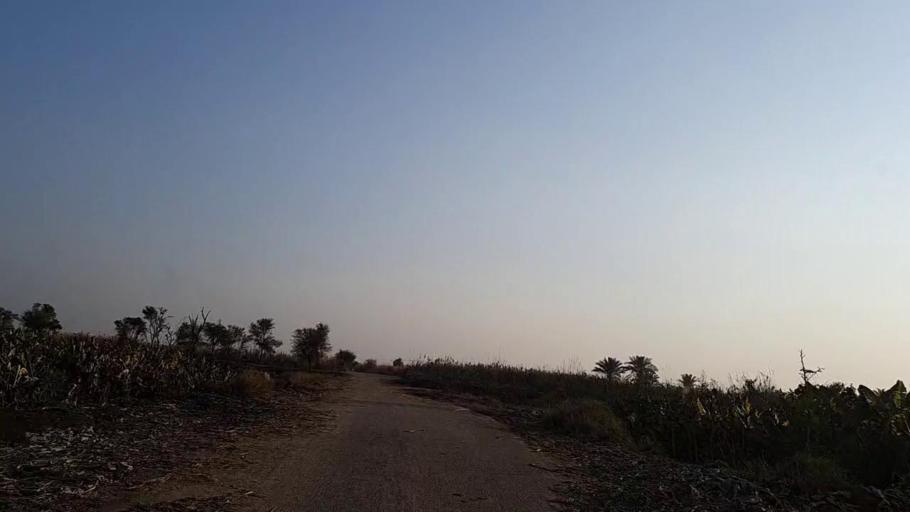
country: PK
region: Sindh
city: Sakrand
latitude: 26.0299
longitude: 68.4379
